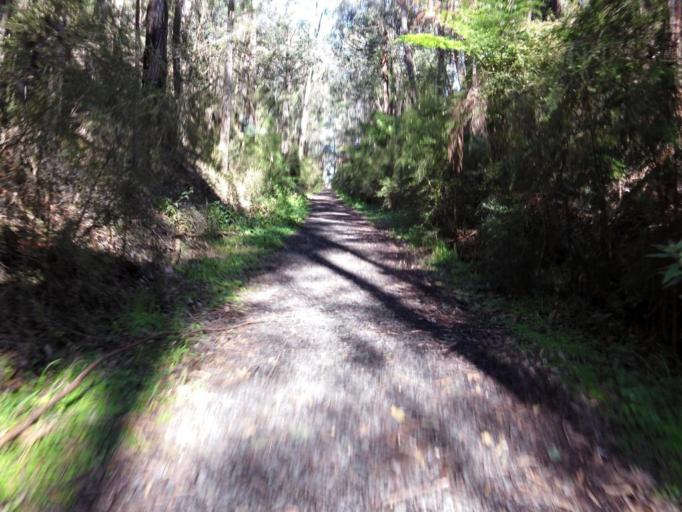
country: AU
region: Victoria
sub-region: Baw Baw
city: Warragul
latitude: -38.0753
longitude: 145.9208
